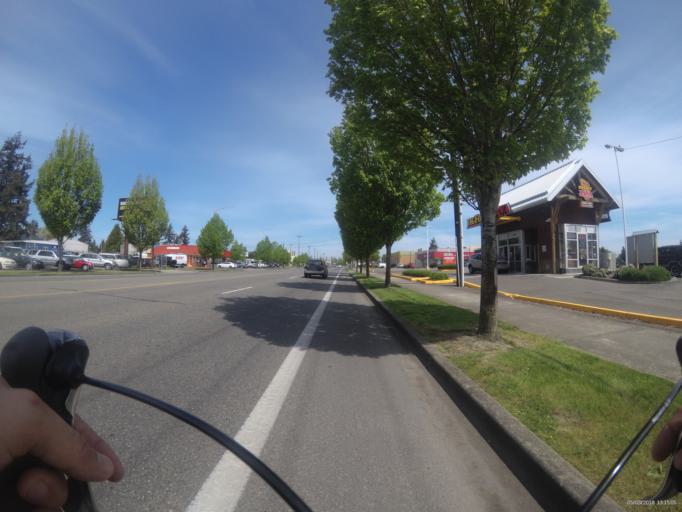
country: US
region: Washington
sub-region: Pierce County
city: McChord Air Force Base
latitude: 47.1580
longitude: -122.4894
